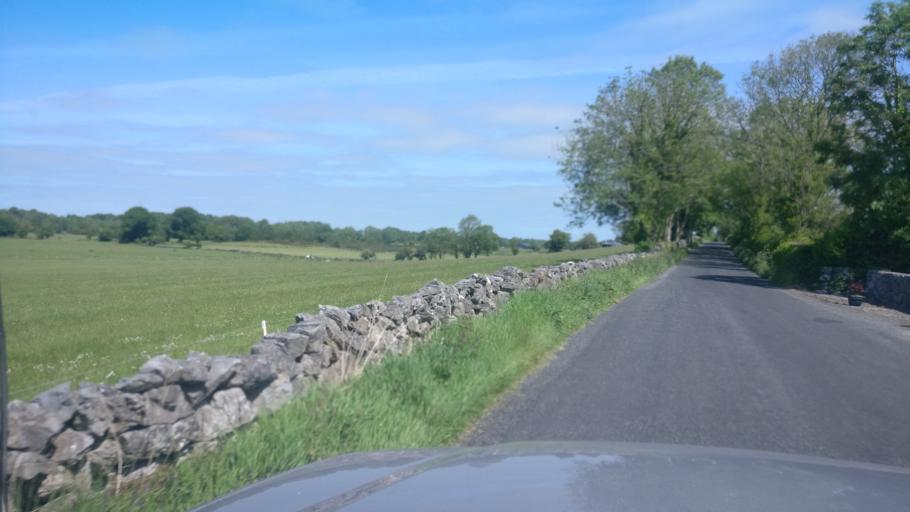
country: IE
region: Connaught
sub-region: County Galway
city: Gort
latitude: 53.1289
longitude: -8.7759
